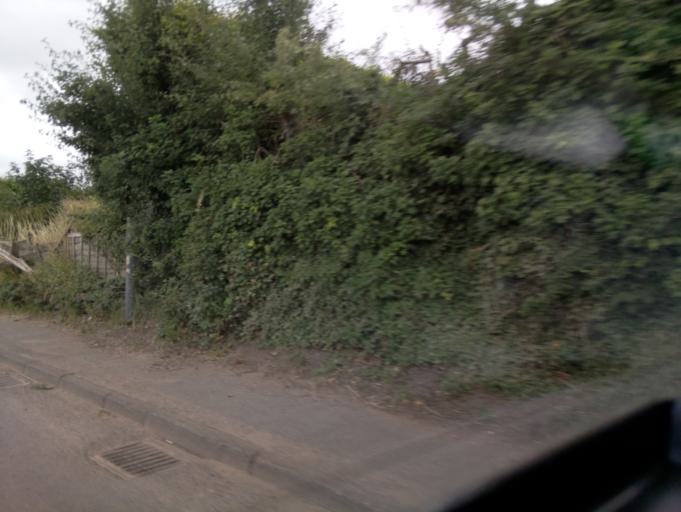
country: GB
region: England
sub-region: Worcestershire
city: Kempsey
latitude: 52.1469
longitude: -2.2155
